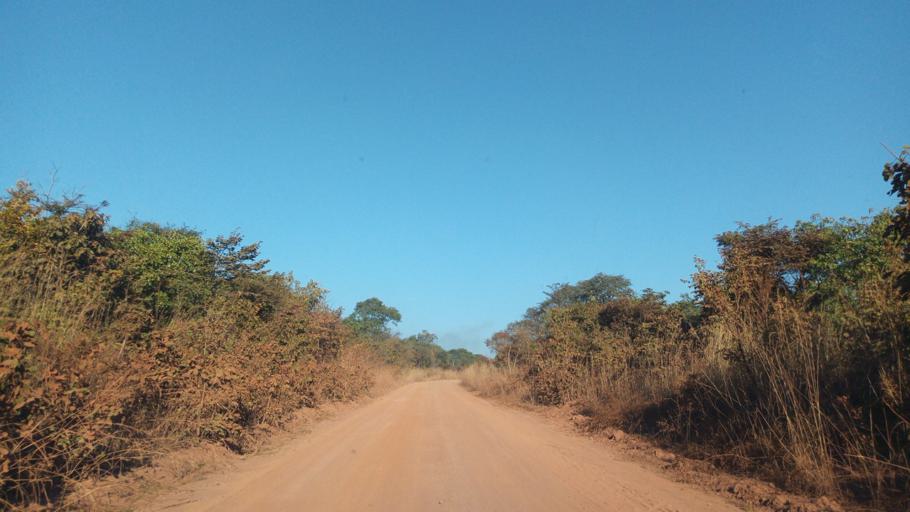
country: ZM
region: Luapula
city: Mwense
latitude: -10.4849
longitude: 28.4980
